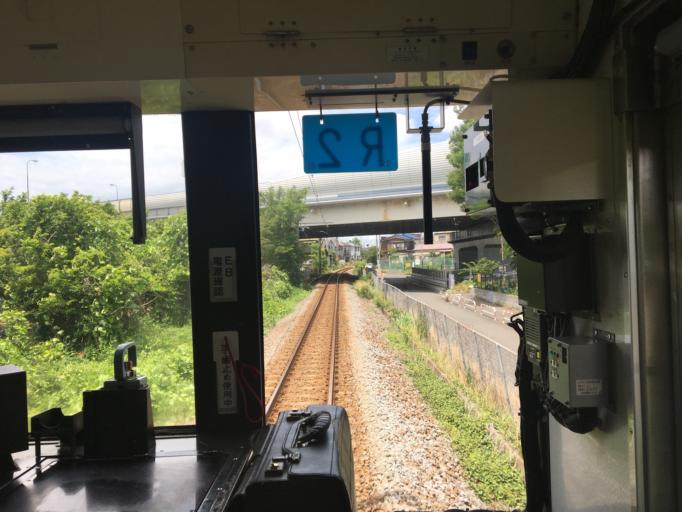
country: JP
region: Kanagawa
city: Chigasaki
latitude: 35.3498
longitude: 139.4018
